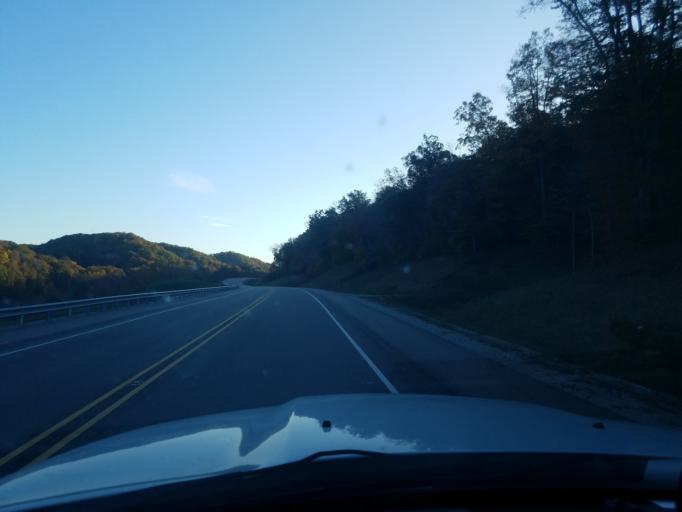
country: US
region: Indiana
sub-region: Washington County
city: New Pekin
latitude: 38.4535
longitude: -85.9328
